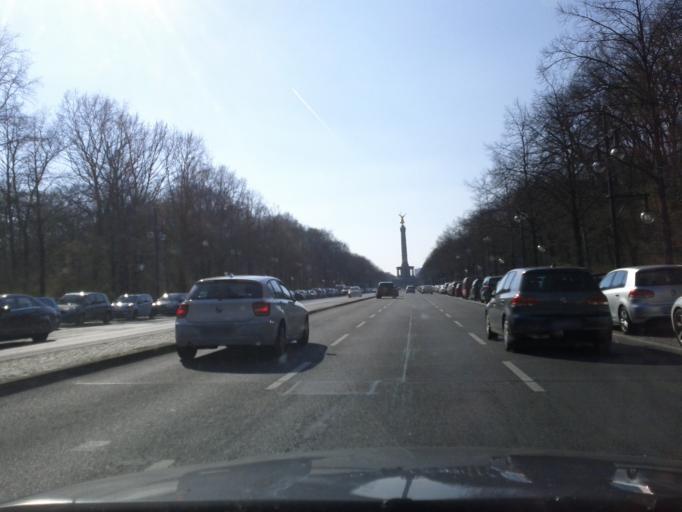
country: DE
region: Berlin
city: Tiergarten Bezirk
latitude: 52.5151
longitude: 13.3585
